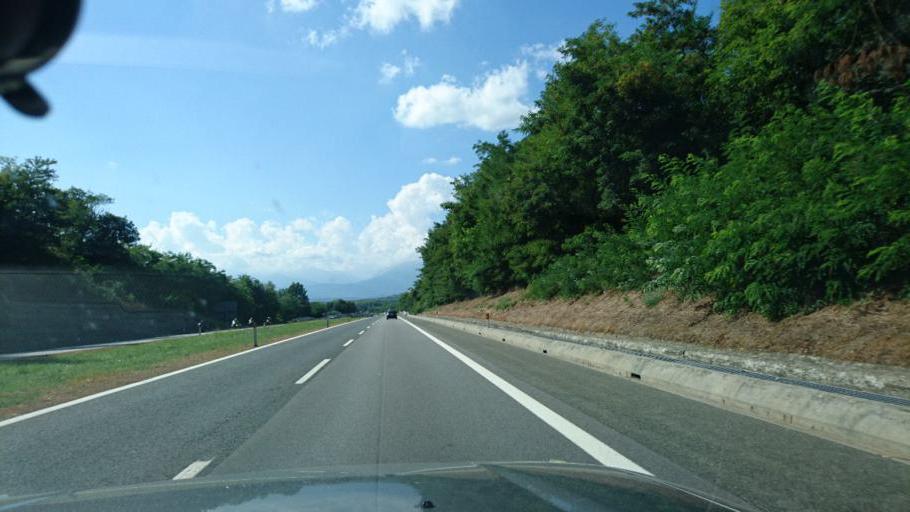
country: IT
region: Piedmont
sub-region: Provincia di Torino
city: Settimo Rottaro
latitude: 45.4107
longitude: 8.0070
